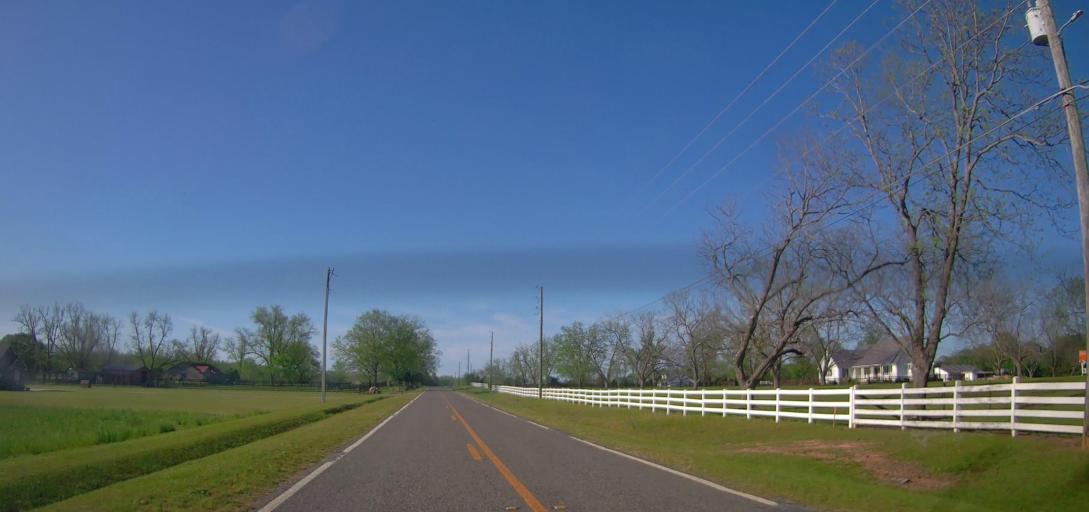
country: US
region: Georgia
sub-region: Houston County
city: Perry
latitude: 32.4726
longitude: -83.8055
